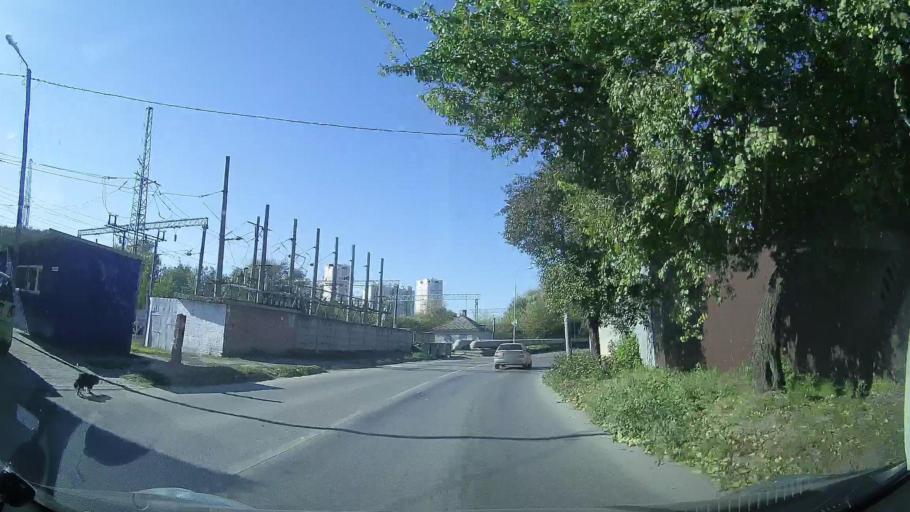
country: RU
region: Rostov
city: Rostov-na-Donu
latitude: 47.2259
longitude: 39.6748
